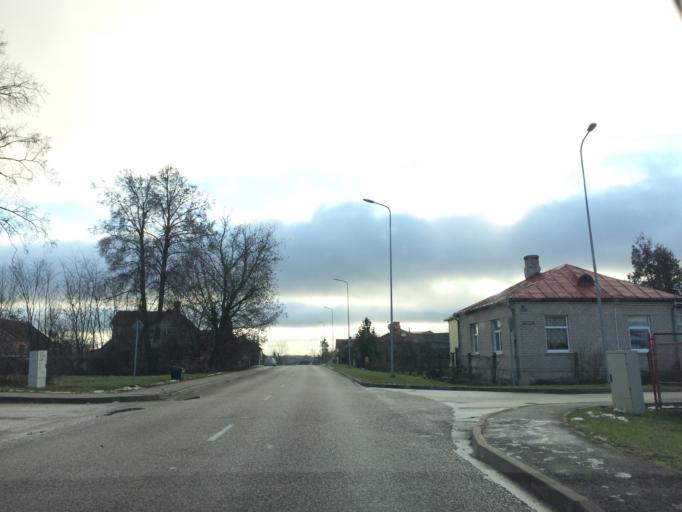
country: LV
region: Rezekne
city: Rezekne
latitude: 56.4945
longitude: 27.3242
